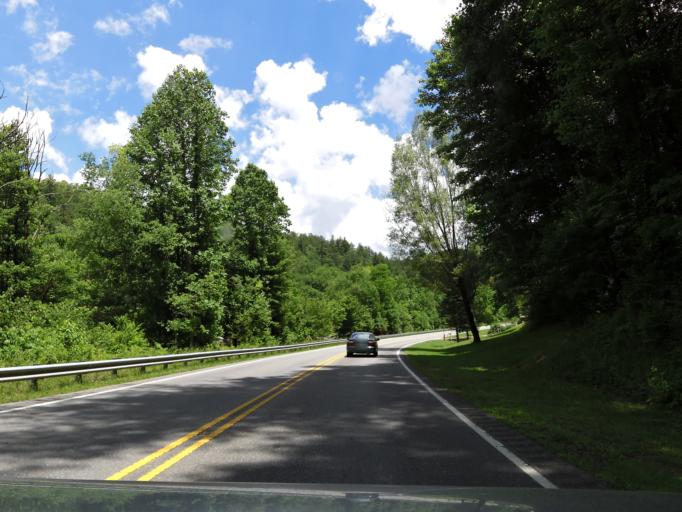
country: US
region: North Carolina
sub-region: Graham County
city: Robbinsville
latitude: 35.2733
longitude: -83.7388
